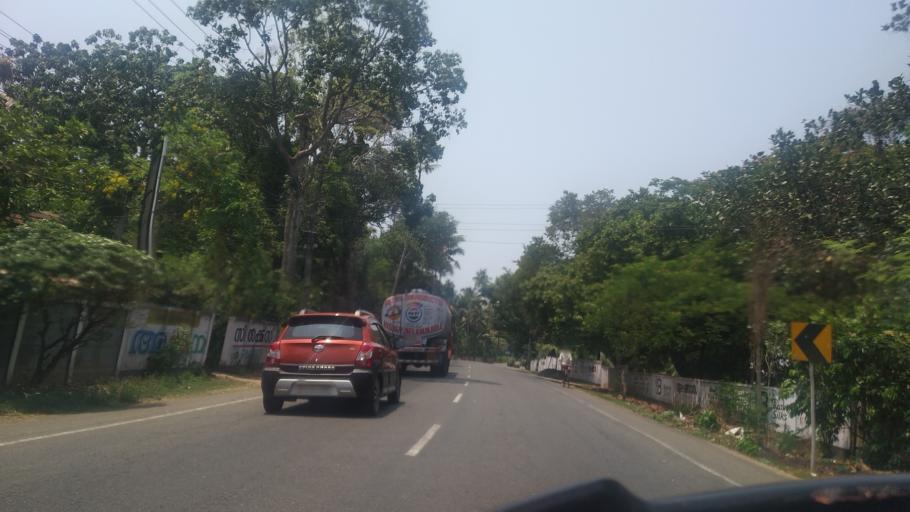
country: IN
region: Kerala
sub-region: Thrissur District
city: Kodungallur
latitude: 10.2715
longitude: 76.1764
